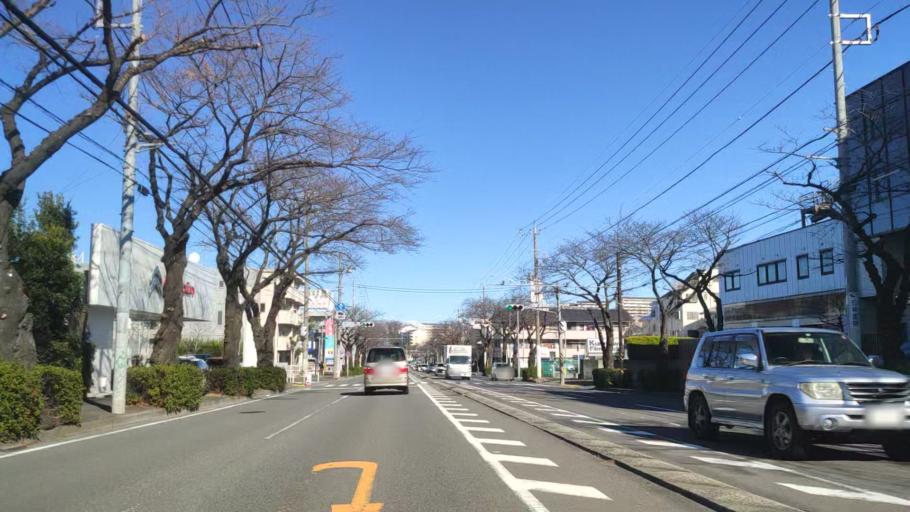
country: JP
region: Tokyo
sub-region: Machida-shi
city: Machida
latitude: 35.5185
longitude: 139.5040
